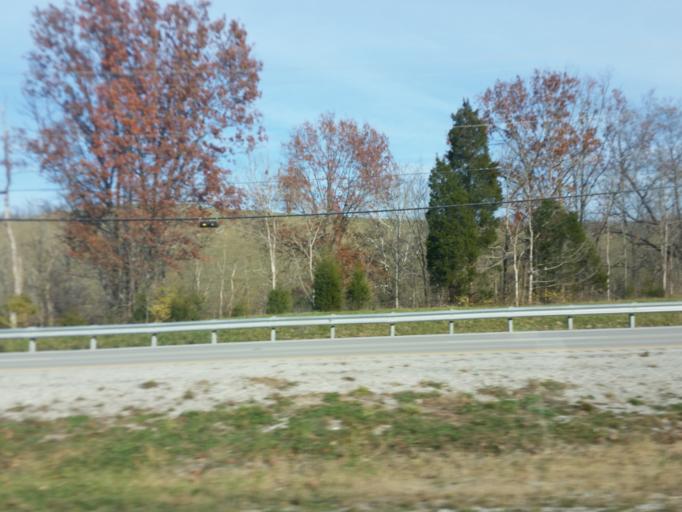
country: US
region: Kentucky
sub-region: Campbell County
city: Claryville
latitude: 38.8667
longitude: -84.3942
